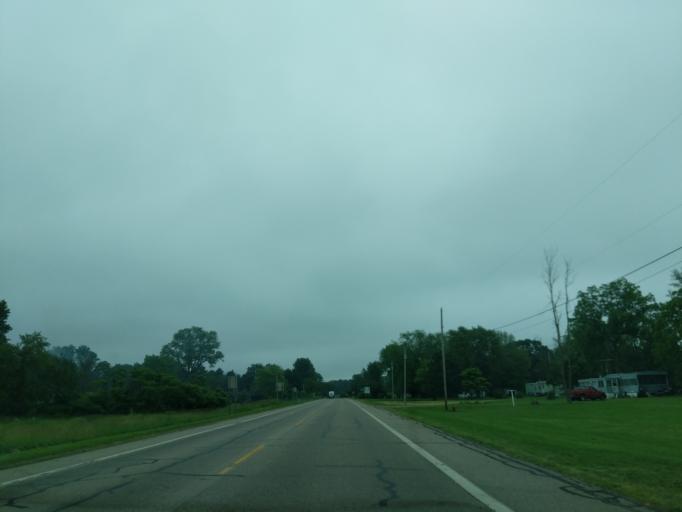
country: US
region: Michigan
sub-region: Hillsdale County
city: Litchfield
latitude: 42.0388
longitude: -84.7448
